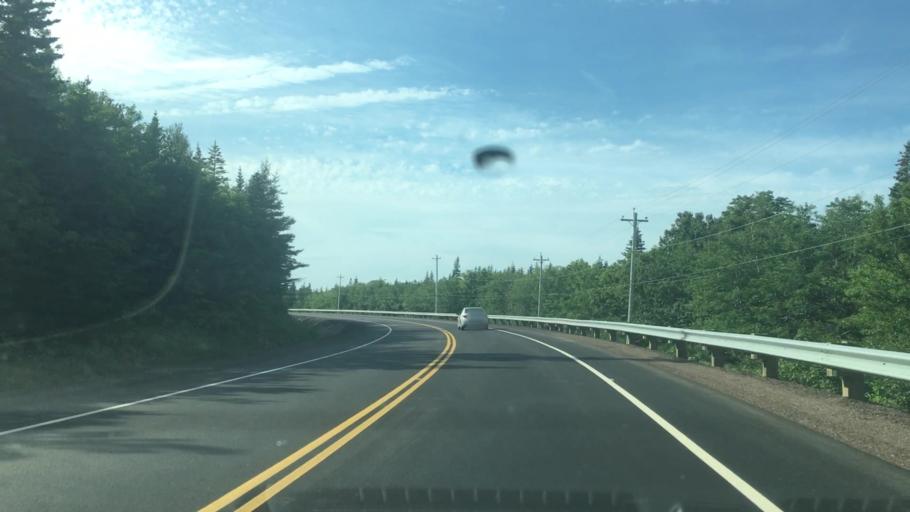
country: CA
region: Nova Scotia
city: Sydney Mines
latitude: 46.8394
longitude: -60.3874
